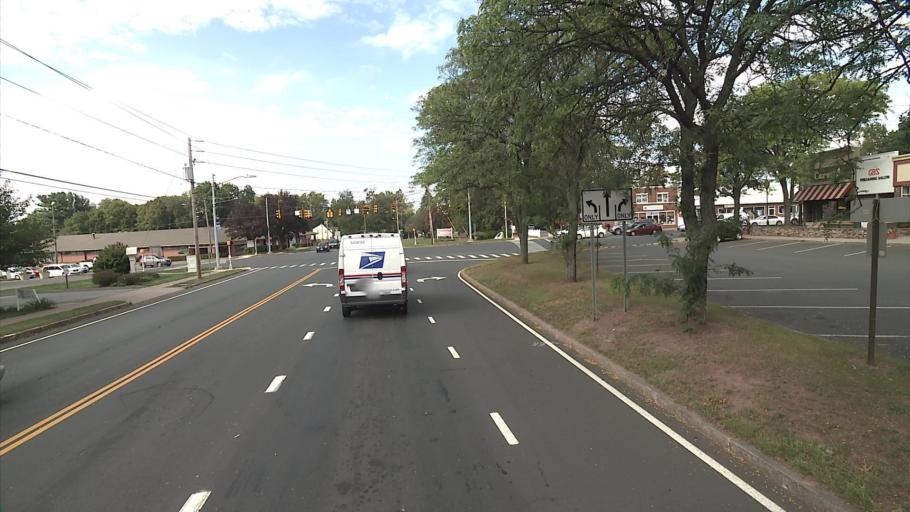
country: US
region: Connecticut
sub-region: Hartford County
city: Newington
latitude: 41.6975
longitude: -72.7235
